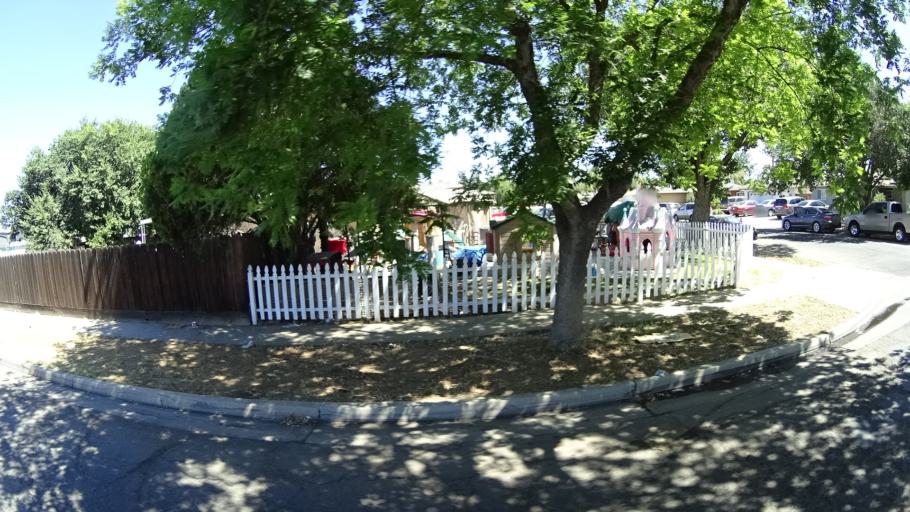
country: US
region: California
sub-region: Fresno County
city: West Park
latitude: 36.7978
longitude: -119.8530
